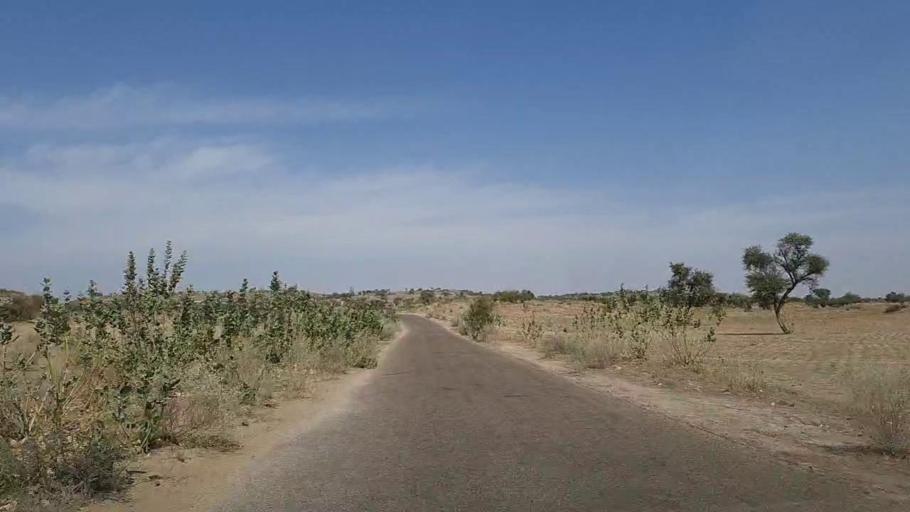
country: PK
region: Sindh
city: Nabisar
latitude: 25.1073
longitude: 69.9968
